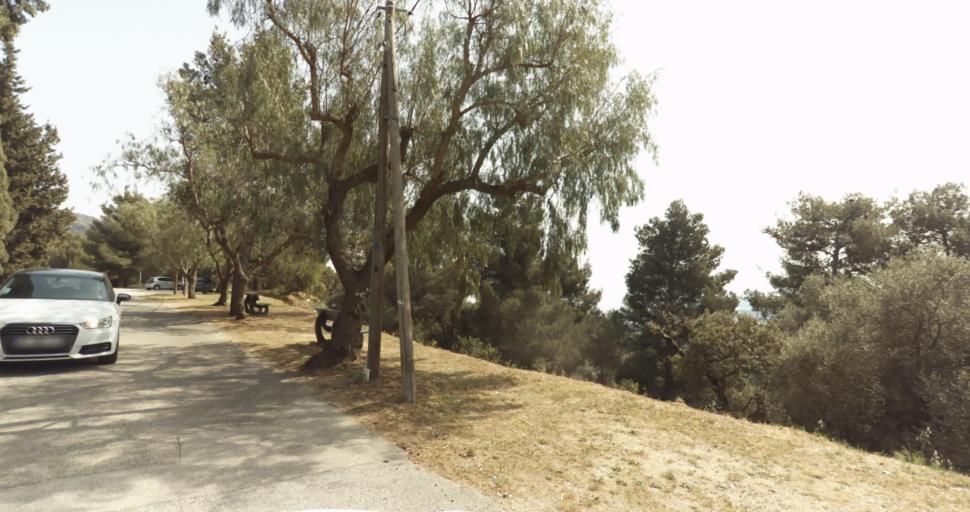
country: FR
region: Provence-Alpes-Cote d'Azur
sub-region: Departement du Var
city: Bormes-les-Mimosas
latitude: 43.1554
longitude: 6.3472
